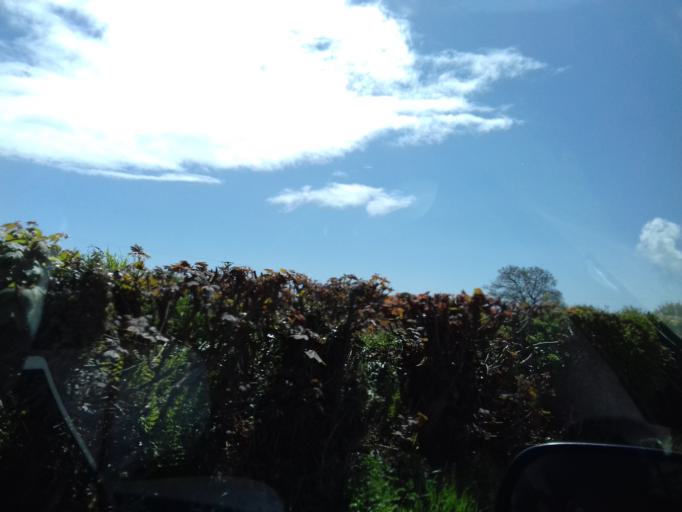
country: IE
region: Munster
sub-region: Waterford
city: Dunmore East
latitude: 52.2317
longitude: -6.8621
